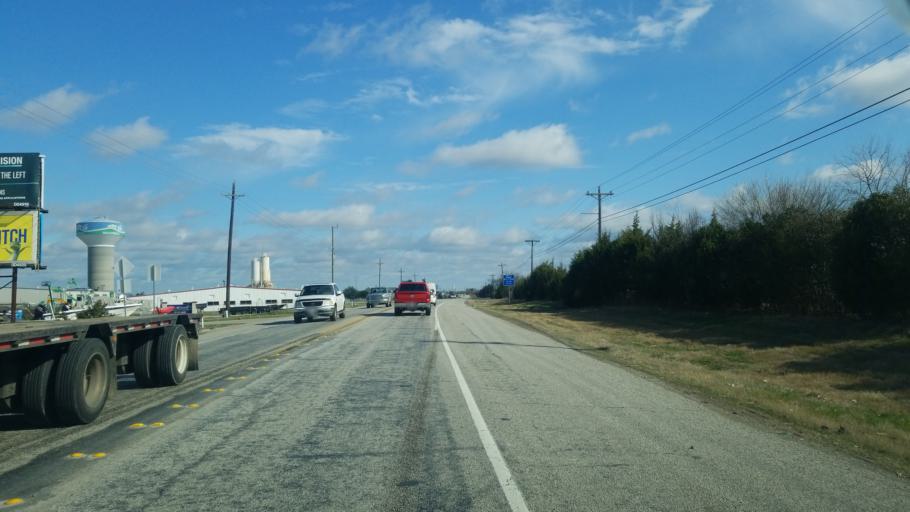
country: US
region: Texas
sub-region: Rockwall County
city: Fate
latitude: 32.9066
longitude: -96.4147
